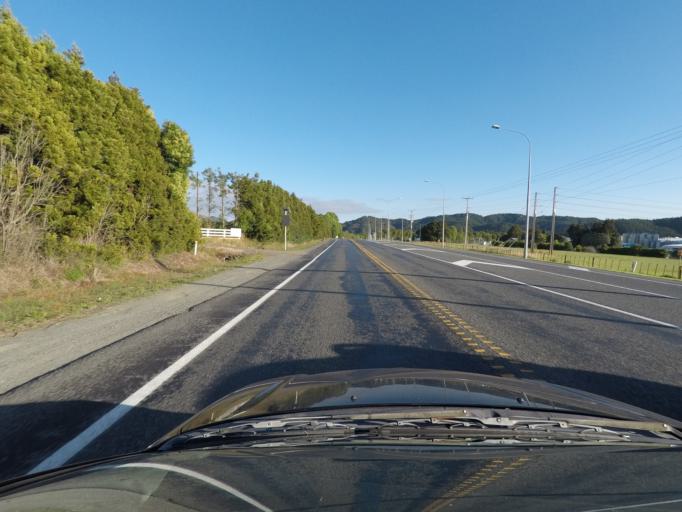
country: NZ
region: Northland
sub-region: Whangarei
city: Whangarei
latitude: -35.6369
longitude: 174.2965
